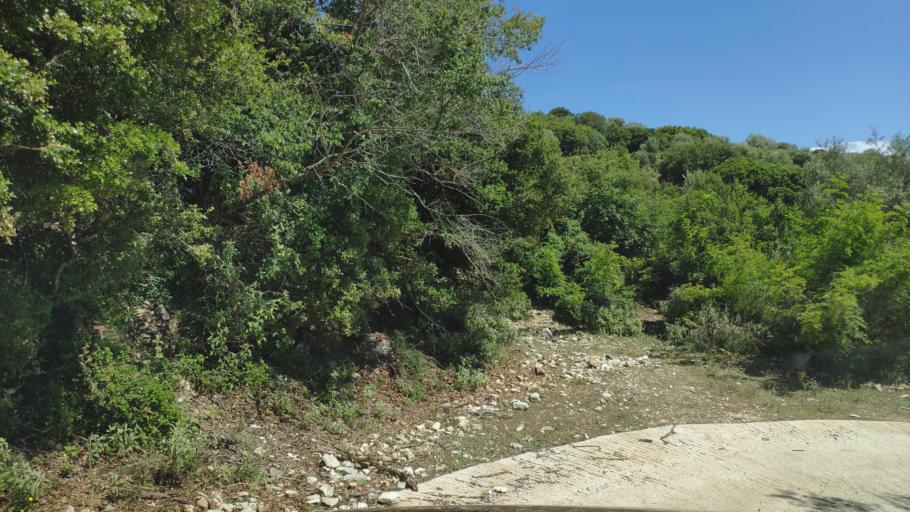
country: AL
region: Vlore
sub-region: Rrethi i Sarandes
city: Konispol
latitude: 39.6365
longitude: 20.2067
